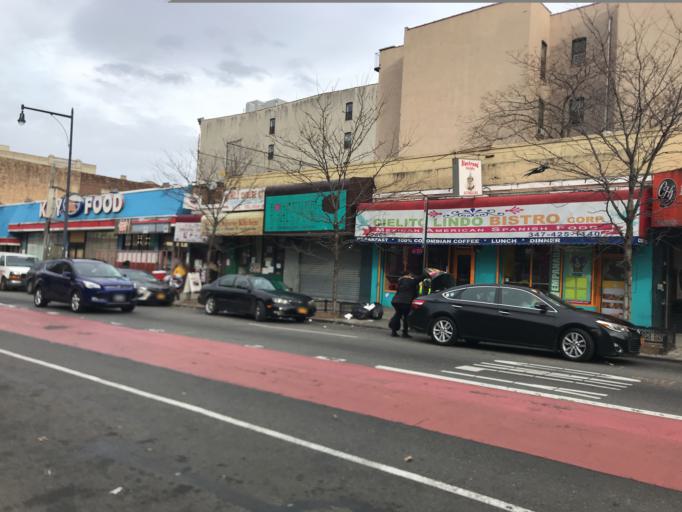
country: US
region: New York
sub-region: Kings County
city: Brooklyn
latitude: 40.6744
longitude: -73.9501
